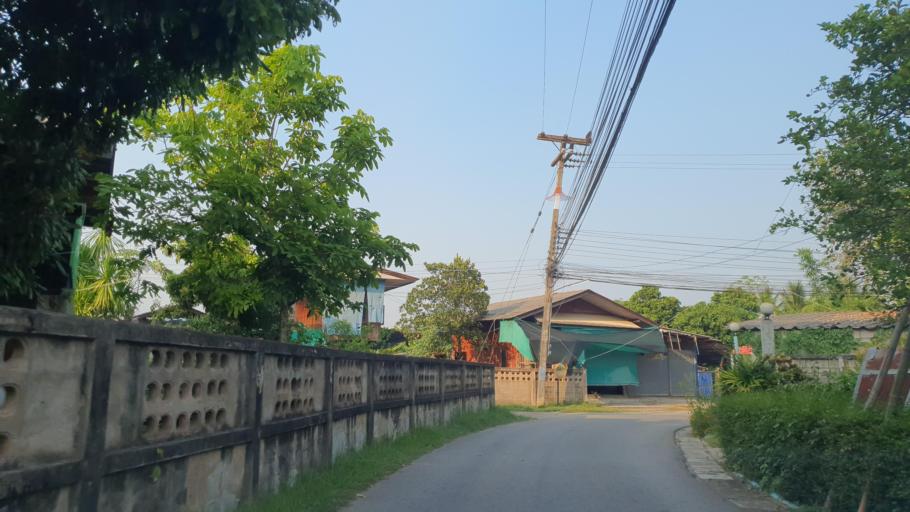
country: TH
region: Chiang Mai
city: San Pa Tong
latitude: 18.6378
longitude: 98.8819
